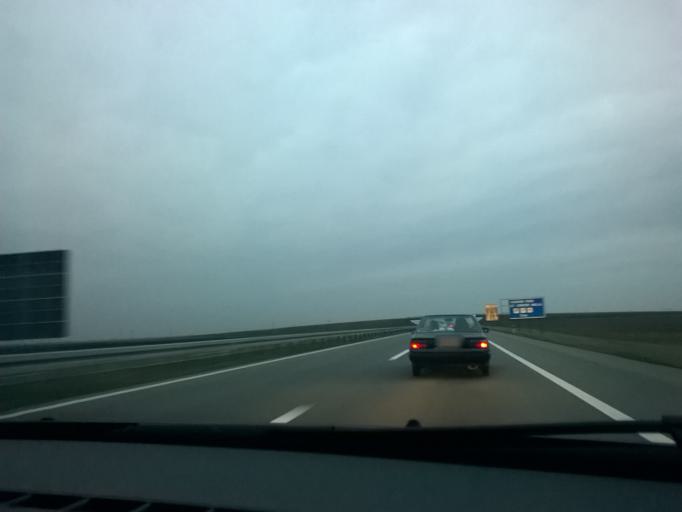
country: RS
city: Krcedin
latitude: 45.0911
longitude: 20.1244
